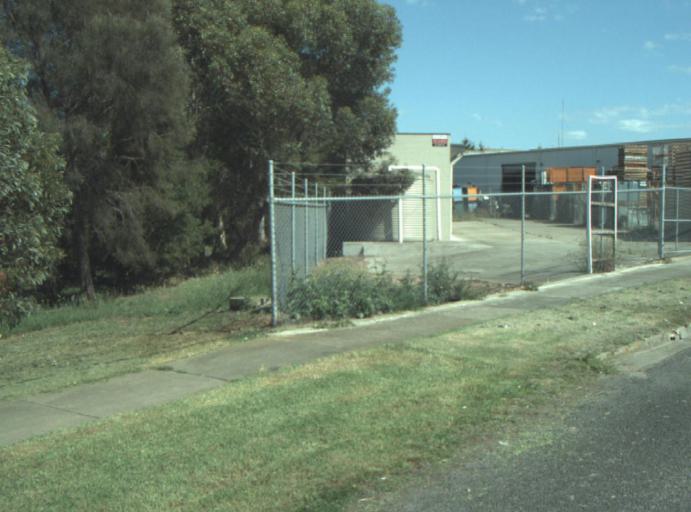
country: AU
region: Victoria
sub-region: Greater Geelong
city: Geelong West
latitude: -38.1257
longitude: 144.3503
